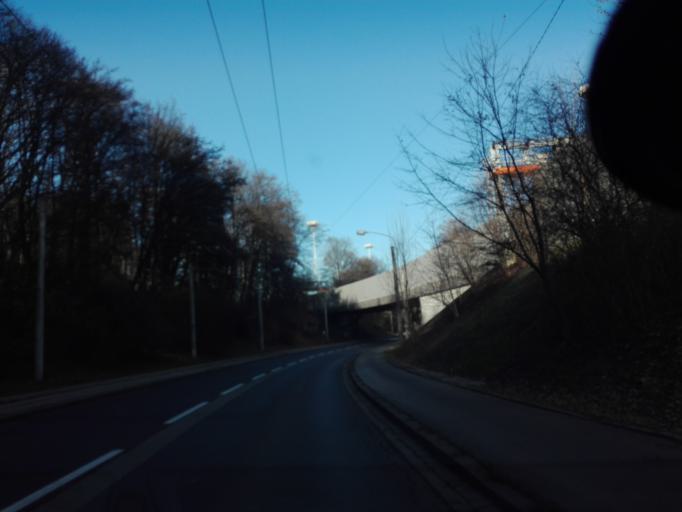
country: AT
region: Upper Austria
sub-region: Linz Stadt
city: Linz
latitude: 48.2768
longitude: 14.2941
